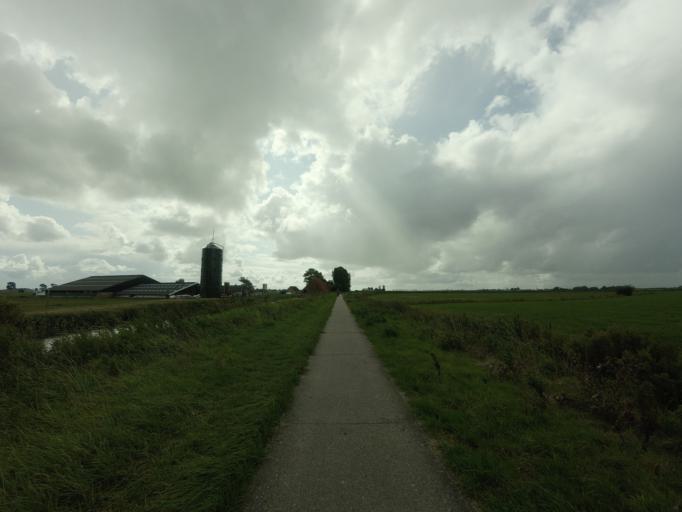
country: NL
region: Friesland
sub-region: Gemeente Boarnsterhim
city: Wergea
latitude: 53.1456
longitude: 5.8245
